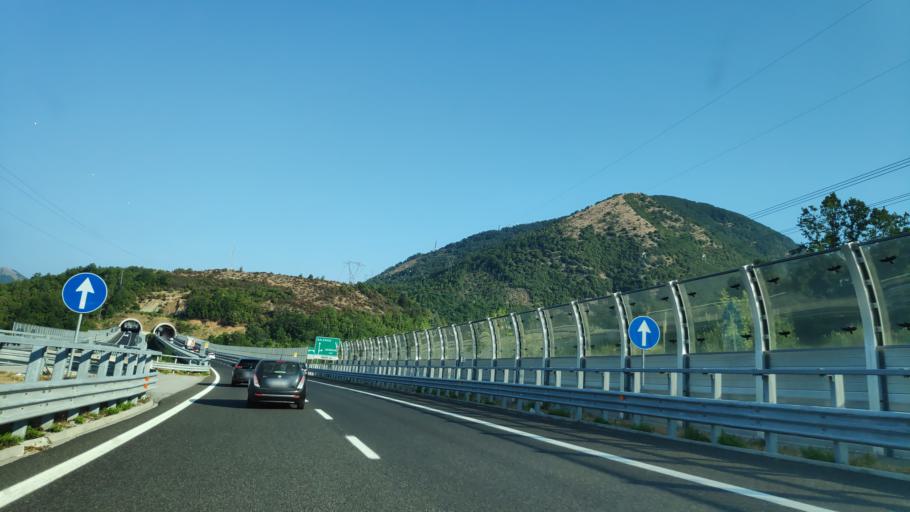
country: IT
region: Basilicate
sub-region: Provincia di Potenza
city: Lagonegro
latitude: 40.1228
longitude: 15.7828
